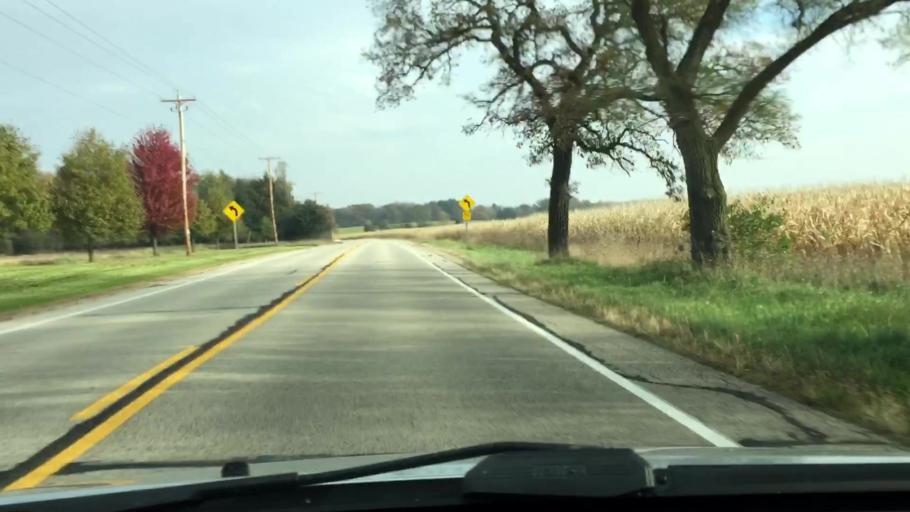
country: US
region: Wisconsin
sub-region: Waukesha County
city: Dousman
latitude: 42.9758
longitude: -88.4689
